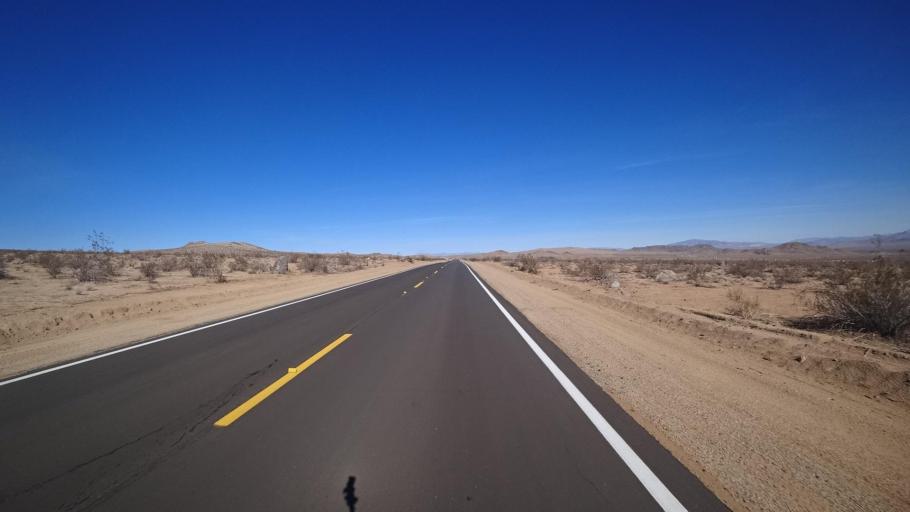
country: US
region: California
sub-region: Kern County
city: Ridgecrest
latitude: 35.5250
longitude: -117.5987
